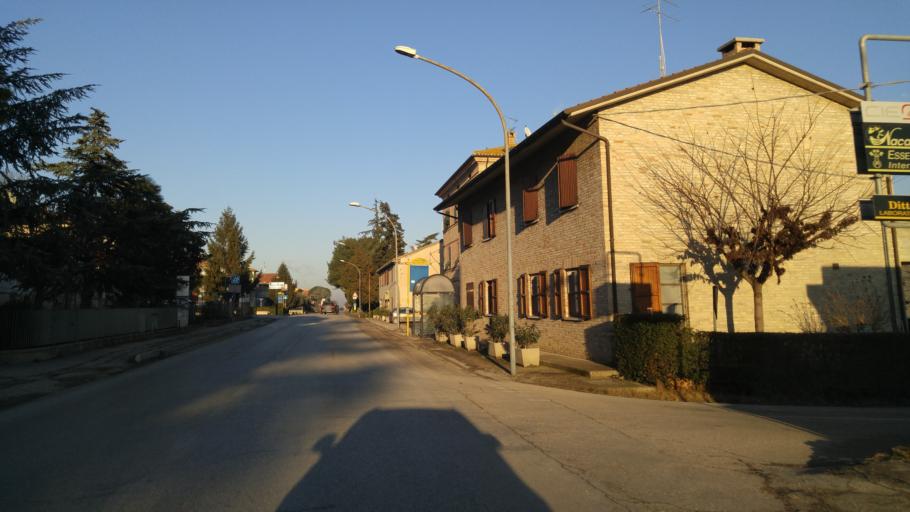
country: IT
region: The Marches
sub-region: Provincia di Pesaro e Urbino
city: Monte Porzio
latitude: 43.6972
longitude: 13.0589
